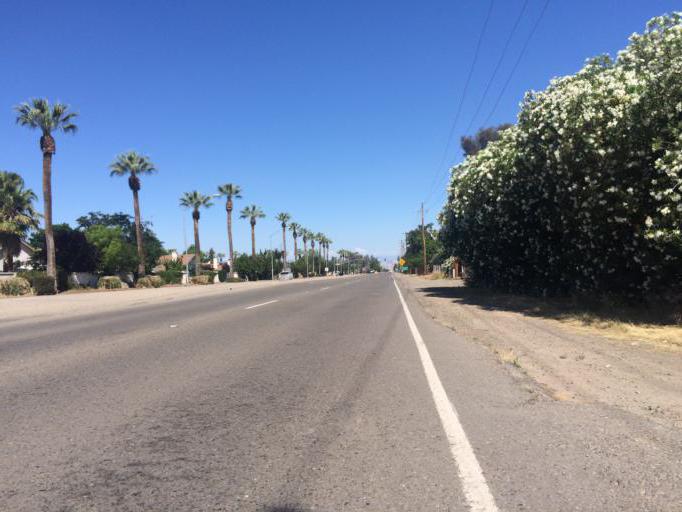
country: US
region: California
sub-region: Fresno County
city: Sunnyside
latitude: 36.7369
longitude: -119.6765
